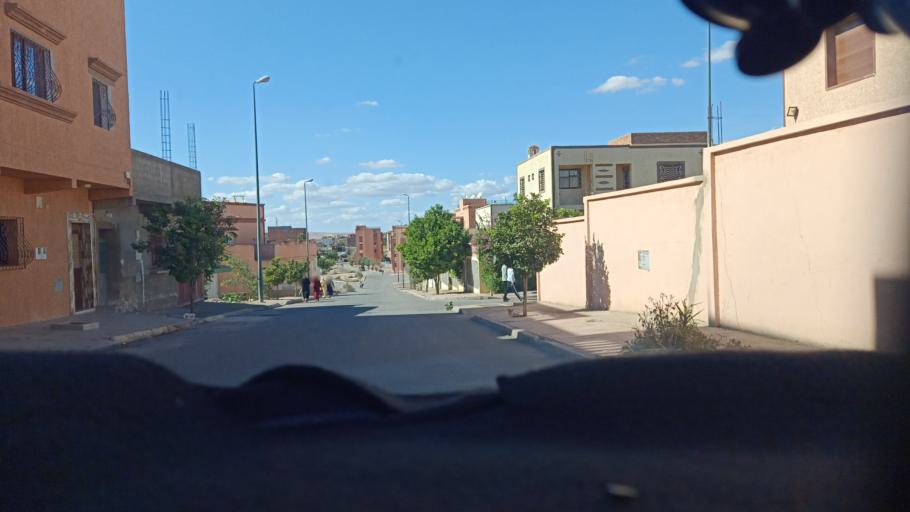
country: MA
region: Doukkala-Abda
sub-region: Safi
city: Youssoufia
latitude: 32.2395
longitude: -8.5329
